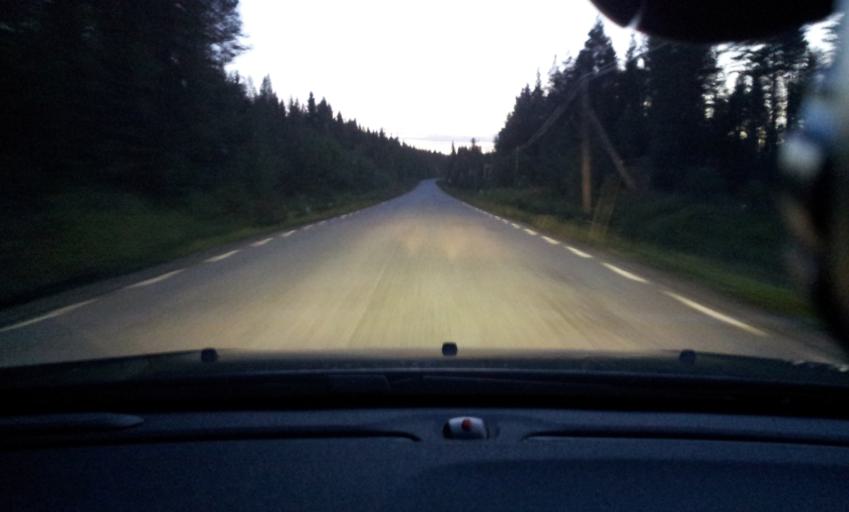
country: SE
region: Jaemtland
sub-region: Bergs Kommun
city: Hoverberg
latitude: 62.7347
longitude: 14.5938
